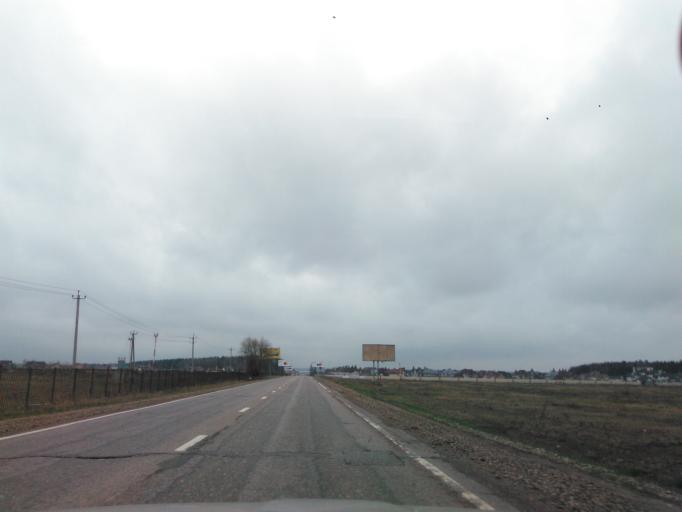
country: RU
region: Moskovskaya
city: Rozhdestveno
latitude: 55.8299
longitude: 37.0319
